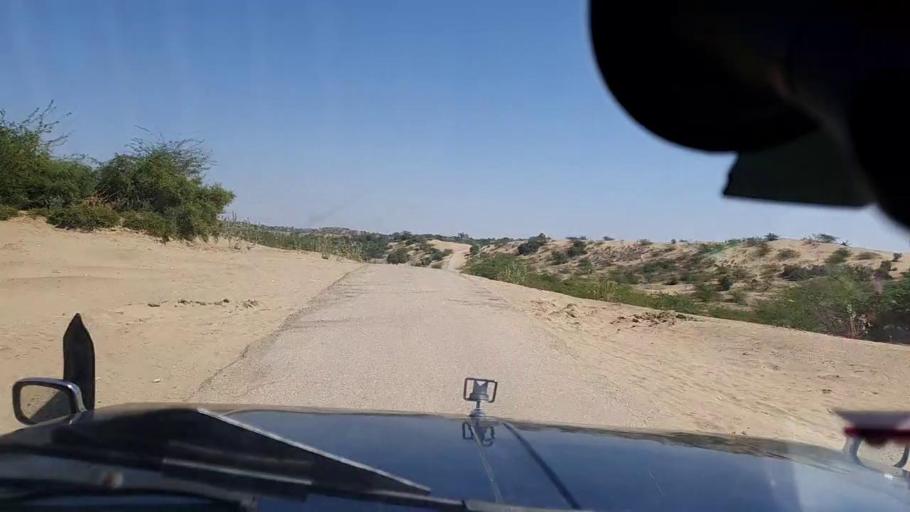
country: PK
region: Sindh
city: Diplo
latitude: 24.5614
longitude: 69.6781
